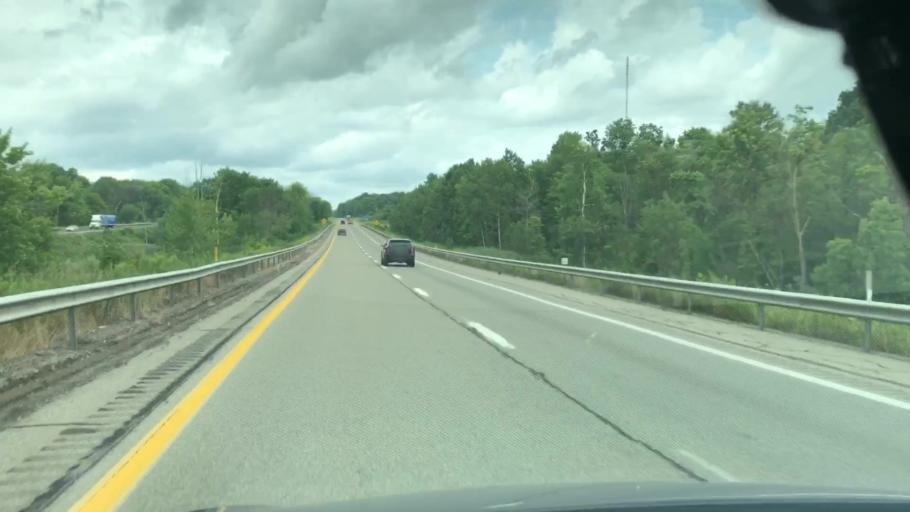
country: US
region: Pennsylvania
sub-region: Erie County
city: Edinboro
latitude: 41.8196
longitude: -80.1753
